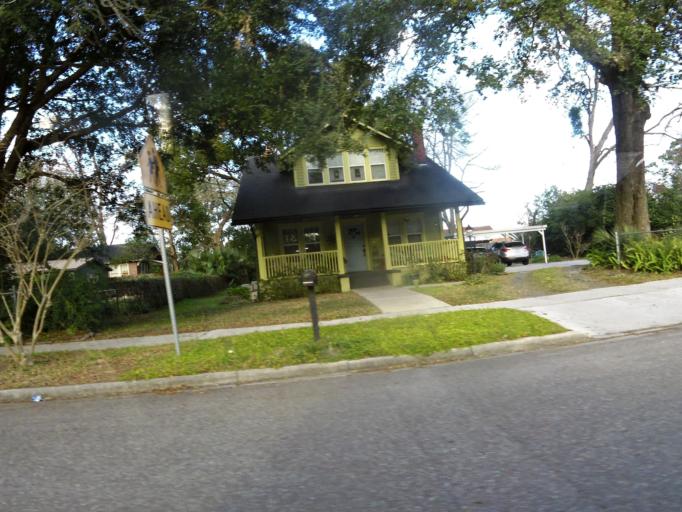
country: US
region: Florida
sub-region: Duval County
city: Jacksonville
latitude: 30.3068
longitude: -81.7187
